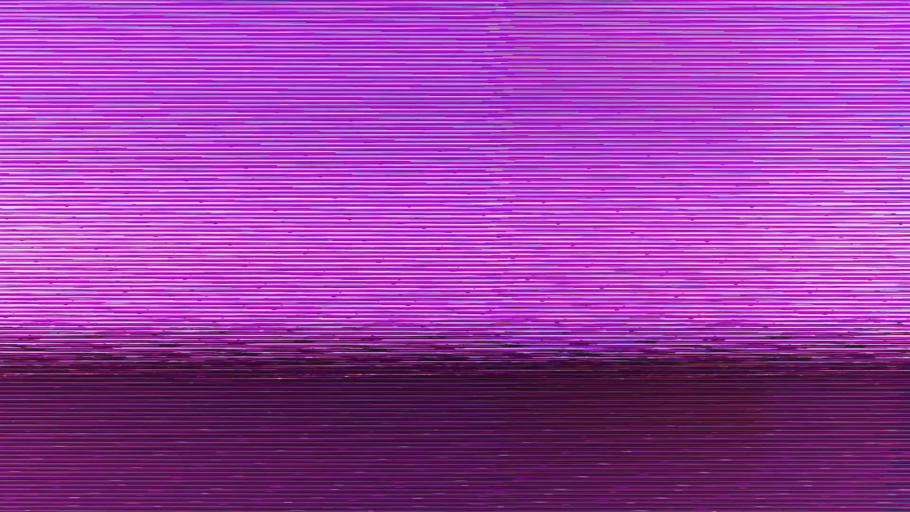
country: US
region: Michigan
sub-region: Oakland County
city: Oxford
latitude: 42.8427
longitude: -83.2753
